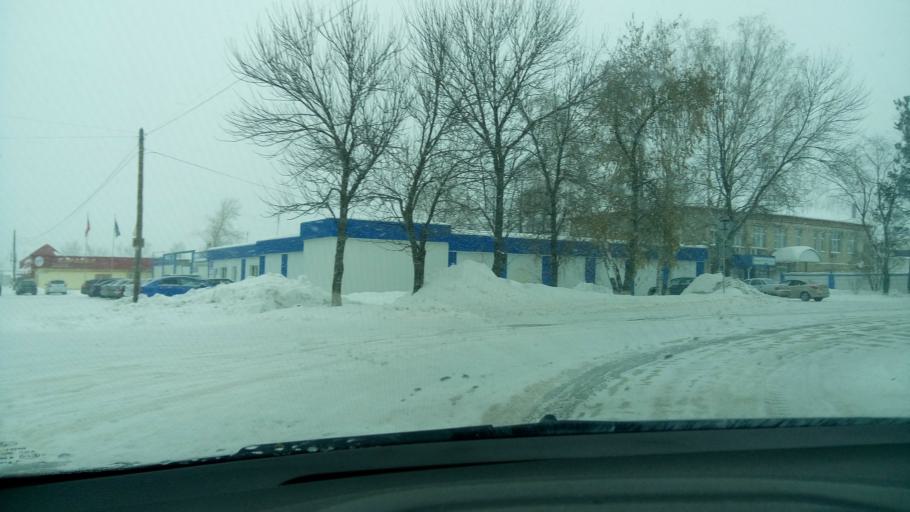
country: RU
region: Sverdlovsk
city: Bogdanovich
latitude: 56.7802
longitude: 62.0240
